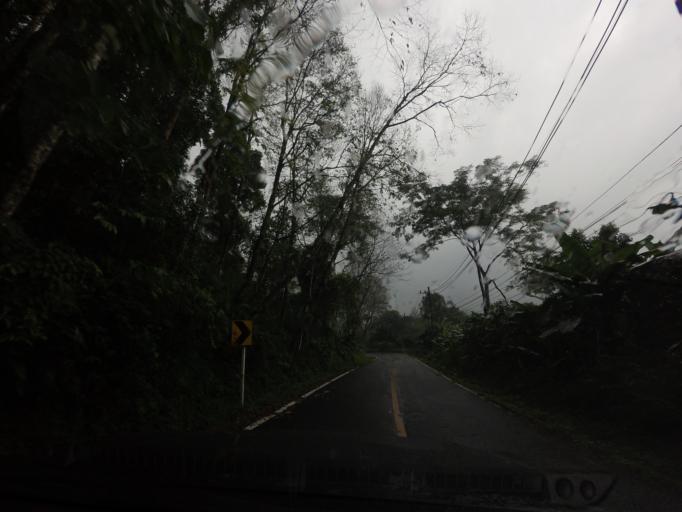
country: TH
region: Nan
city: Bo Kluea
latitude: 19.1822
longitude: 101.0916
